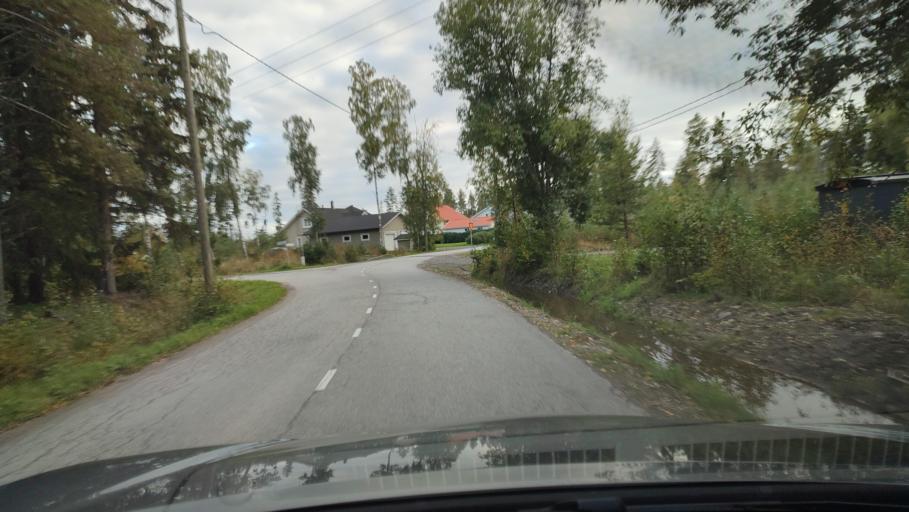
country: FI
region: Ostrobothnia
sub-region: Sydosterbotten
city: Kristinestad
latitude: 62.2571
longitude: 21.3841
